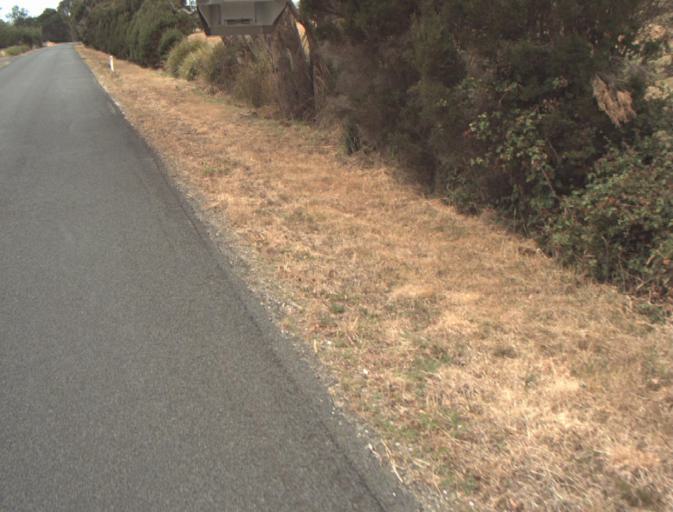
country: AU
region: Tasmania
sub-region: Launceston
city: Mayfield
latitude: -41.2128
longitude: 147.0554
